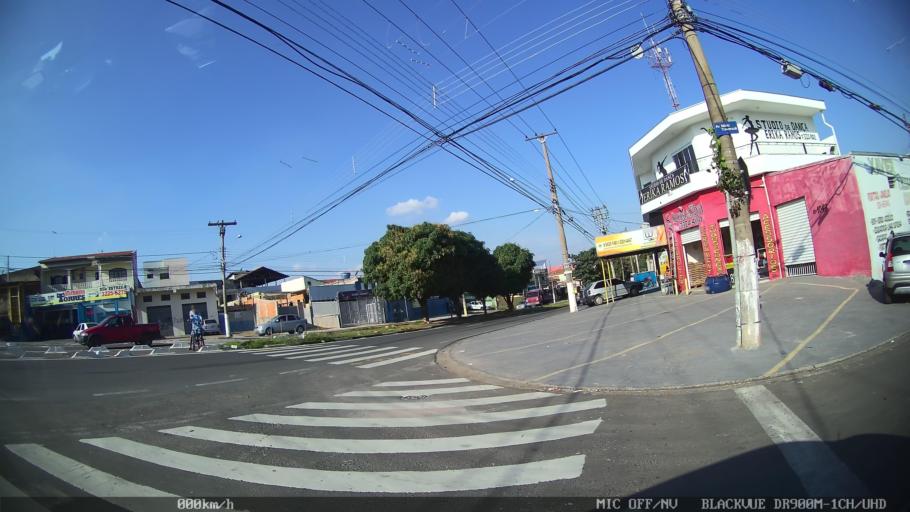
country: BR
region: Sao Paulo
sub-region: Campinas
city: Campinas
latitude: -22.9892
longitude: -47.1414
